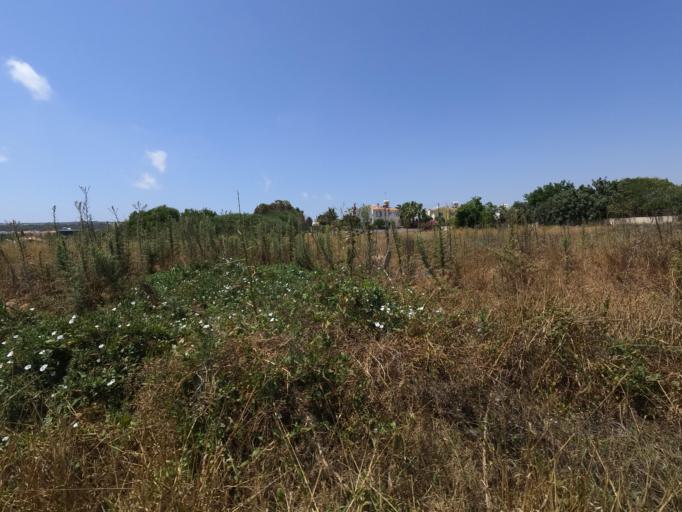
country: CY
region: Ammochostos
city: Protaras
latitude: 35.0278
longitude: 34.0342
